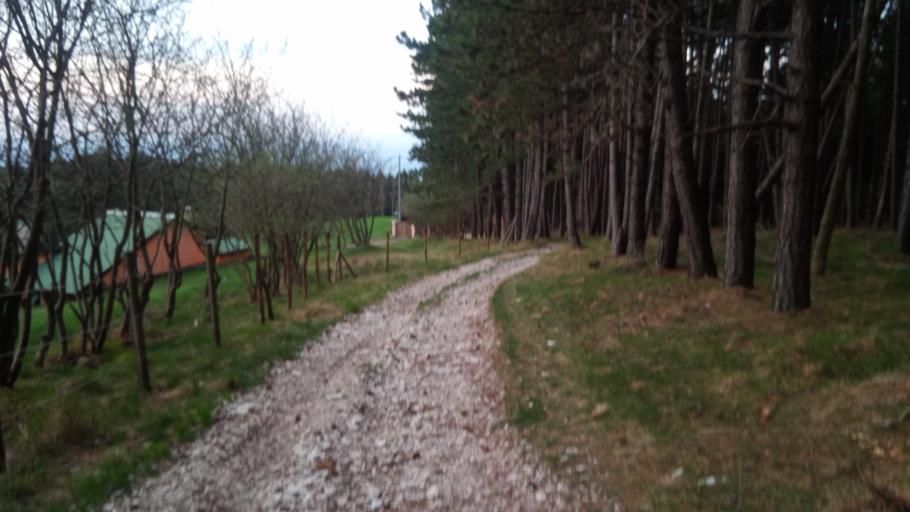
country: IT
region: Veneto
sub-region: Provincia di Vicenza
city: Conco
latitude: 45.8082
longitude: 11.6233
